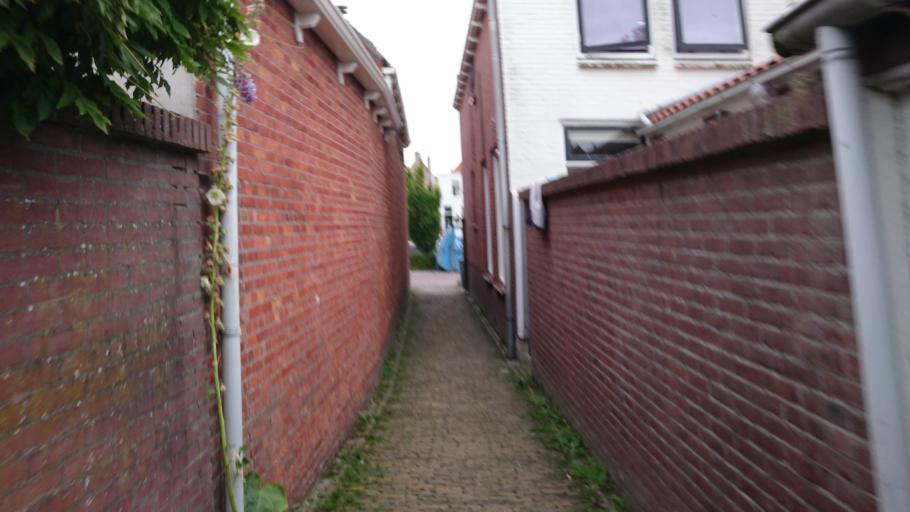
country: NL
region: Zeeland
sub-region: Schouwen-Duiveland
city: Scharendijke
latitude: 51.7265
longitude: 3.9137
